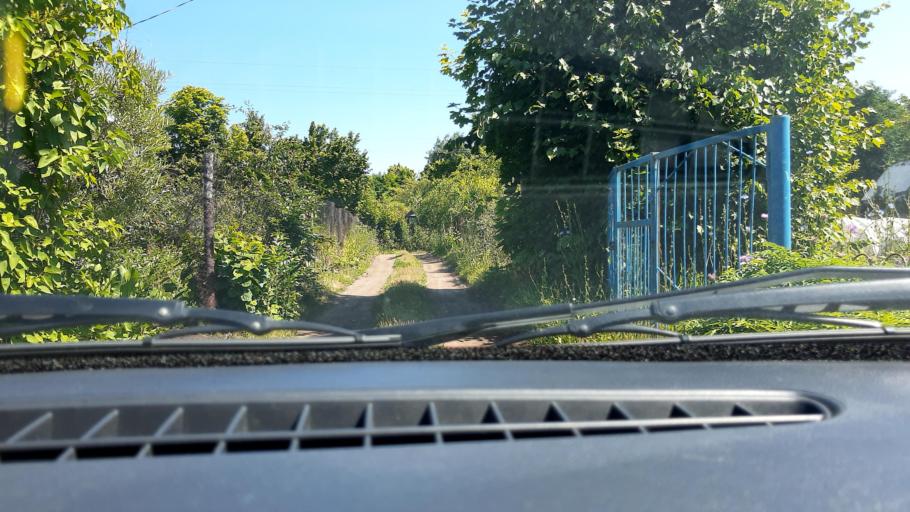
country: RU
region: Bashkortostan
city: Karmaskaly
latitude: 54.3630
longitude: 55.8907
